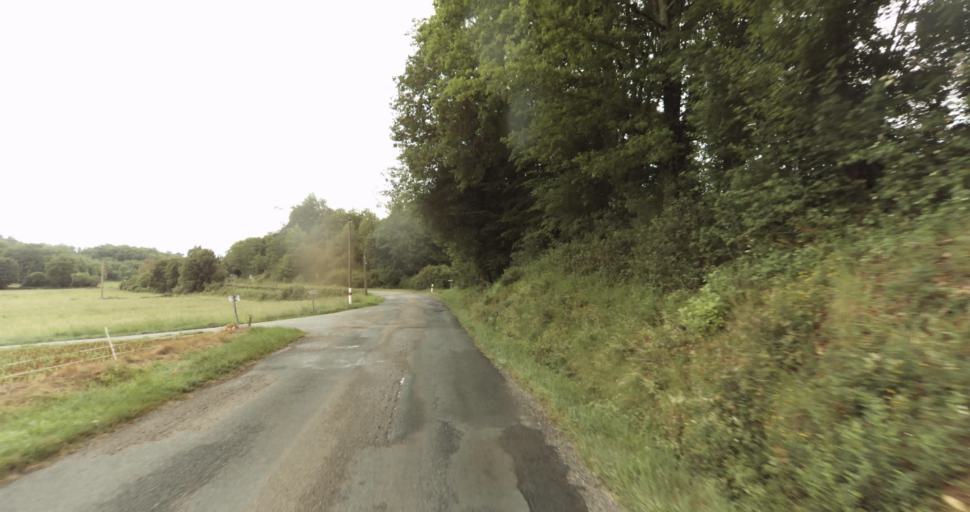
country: FR
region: Aquitaine
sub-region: Departement de la Dordogne
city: Belves
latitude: 44.7549
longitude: 0.9282
